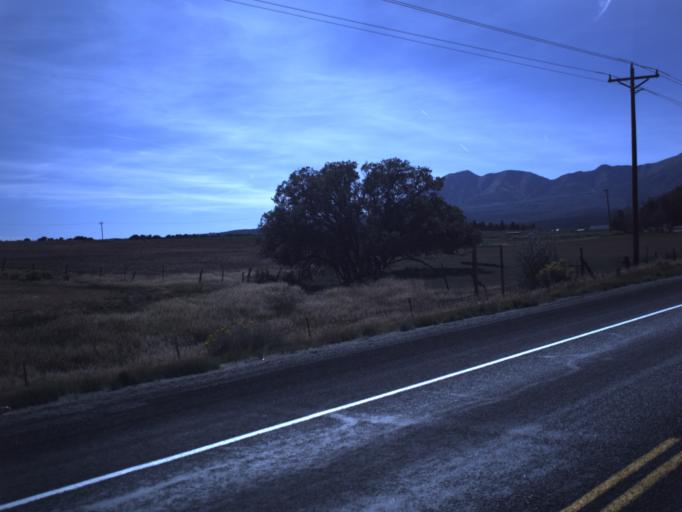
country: US
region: Utah
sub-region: San Juan County
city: Monticello
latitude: 37.8728
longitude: -109.3207
